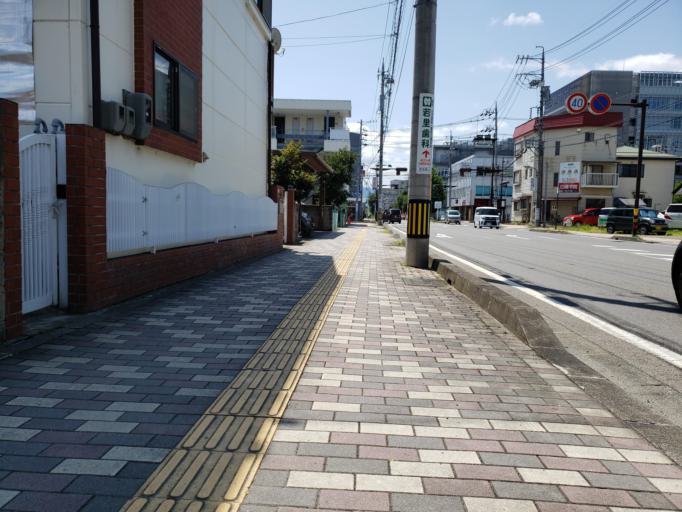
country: JP
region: Nagano
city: Nagano-shi
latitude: 36.6326
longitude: 138.1911
